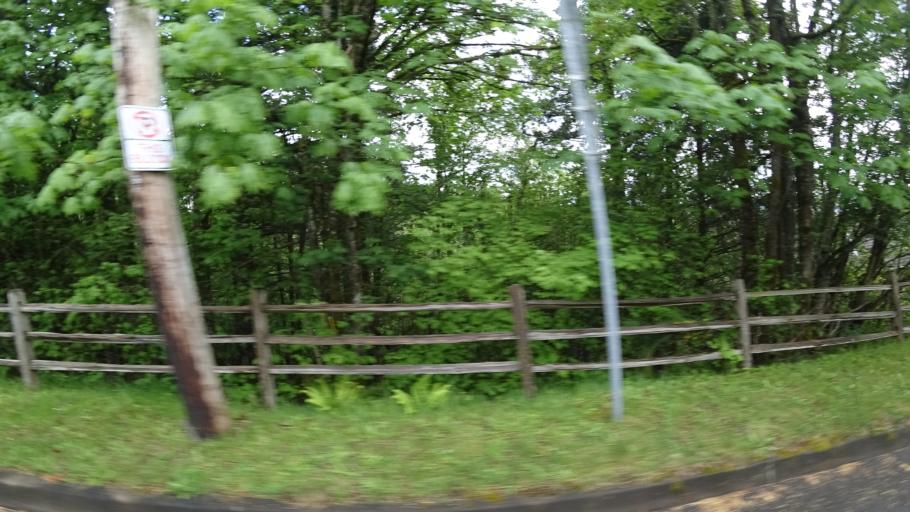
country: US
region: Oregon
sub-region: Washington County
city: West Haven
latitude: 45.5463
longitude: -122.7717
